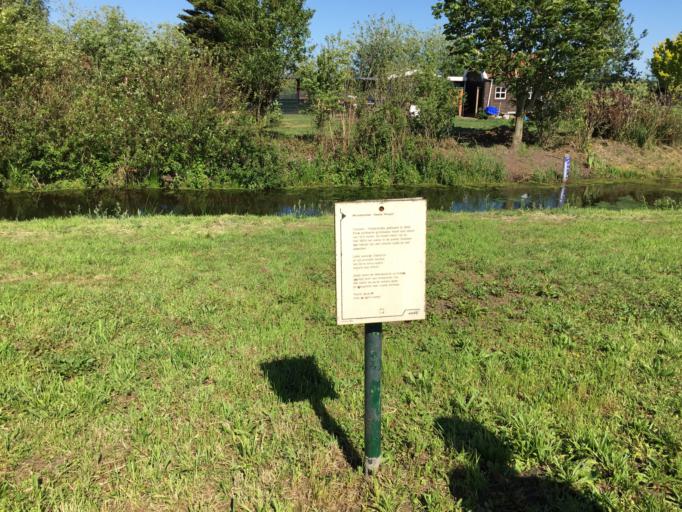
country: NL
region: Friesland
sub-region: Gemeente Leeuwarden
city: Camminghaburen
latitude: 53.2001
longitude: 5.8668
